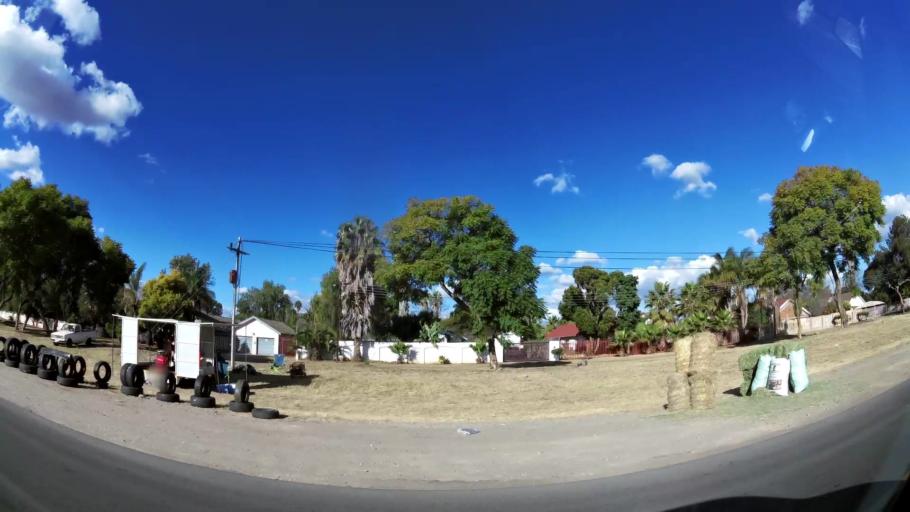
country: ZA
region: Limpopo
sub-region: Capricorn District Municipality
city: Polokwane
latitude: -23.9305
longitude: 29.4504
